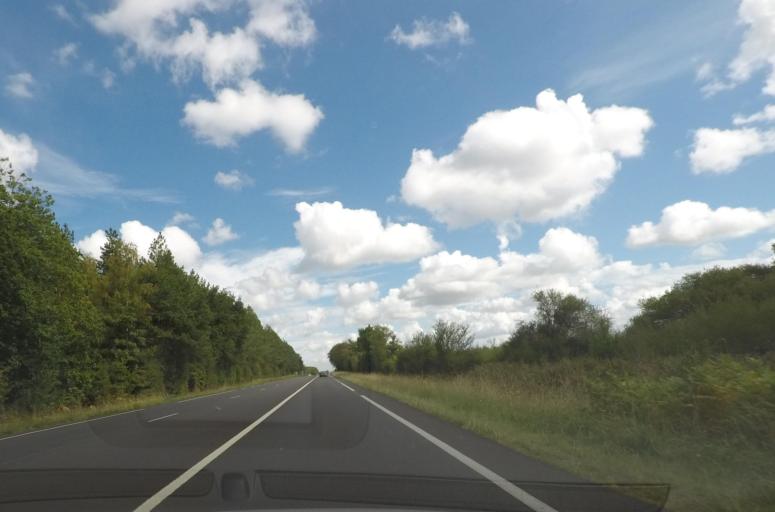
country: FR
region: Pays de la Loire
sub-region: Departement de la Sarthe
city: Clermont-Creans
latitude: 47.7589
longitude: 0.0127
